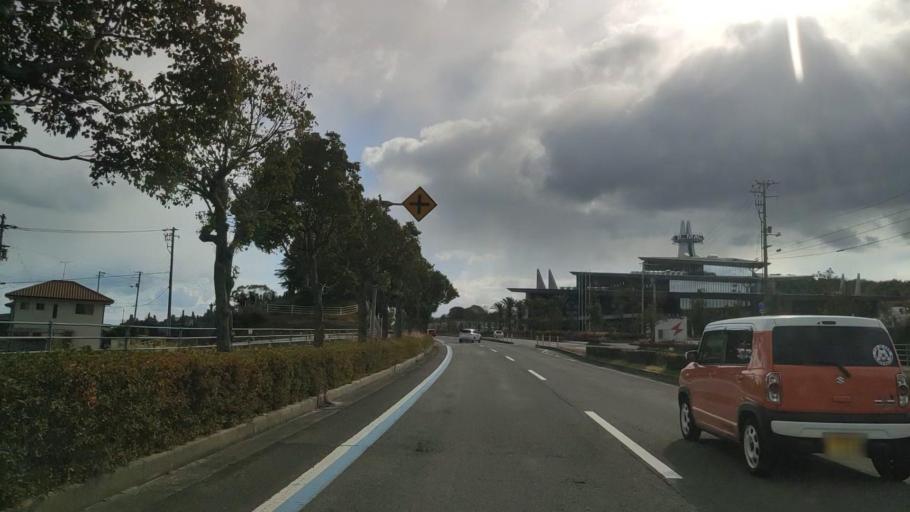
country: JP
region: Ehime
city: Hojo
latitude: 34.0647
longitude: 132.9525
